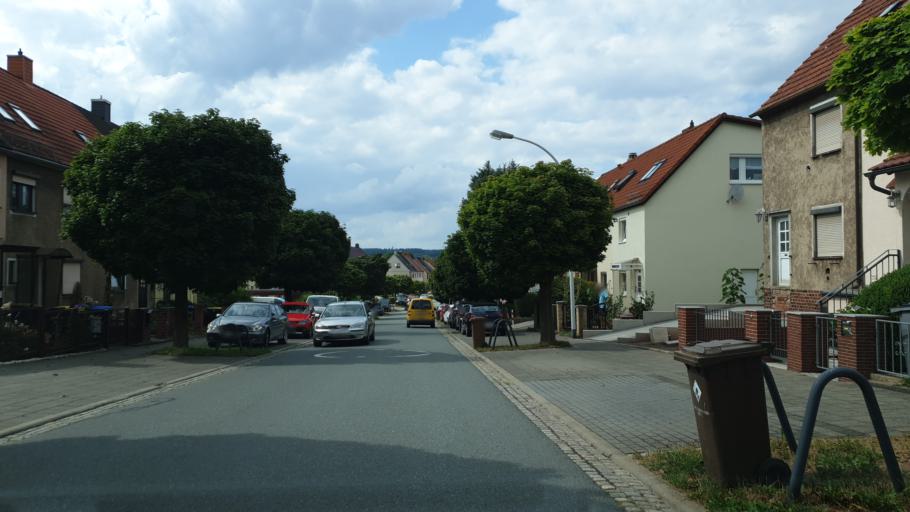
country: DE
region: Saxony
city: Neukirchen
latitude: 50.8069
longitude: 12.8373
